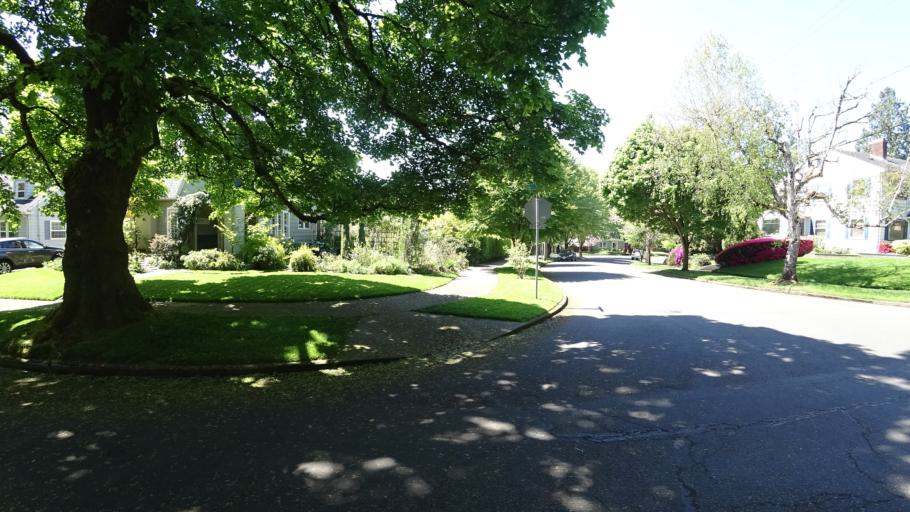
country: US
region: Oregon
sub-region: Clackamas County
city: Milwaukie
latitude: 45.4724
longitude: -122.6262
